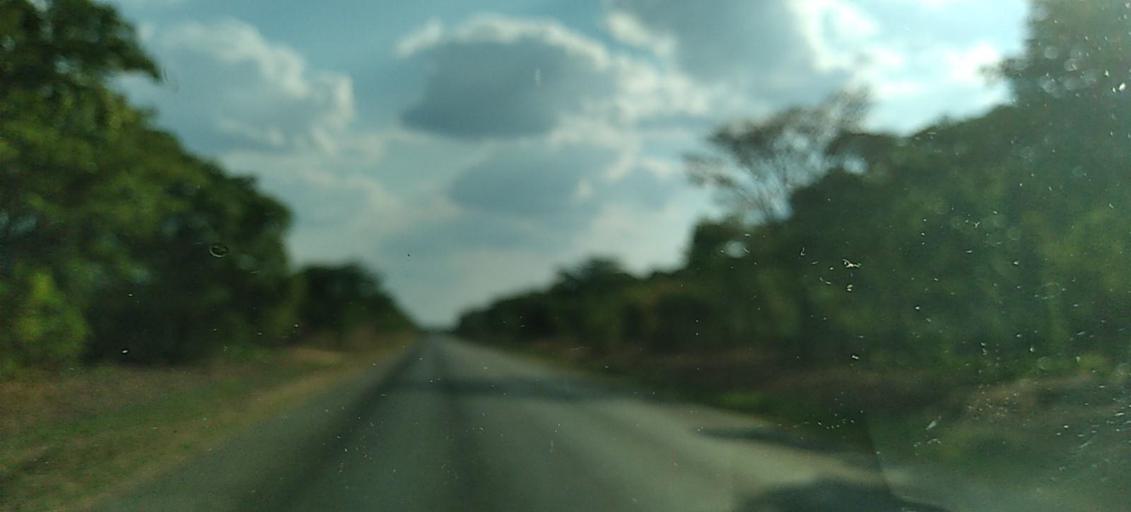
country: ZM
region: Copperbelt
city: Luanshya
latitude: -13.3817
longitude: 28.3926
